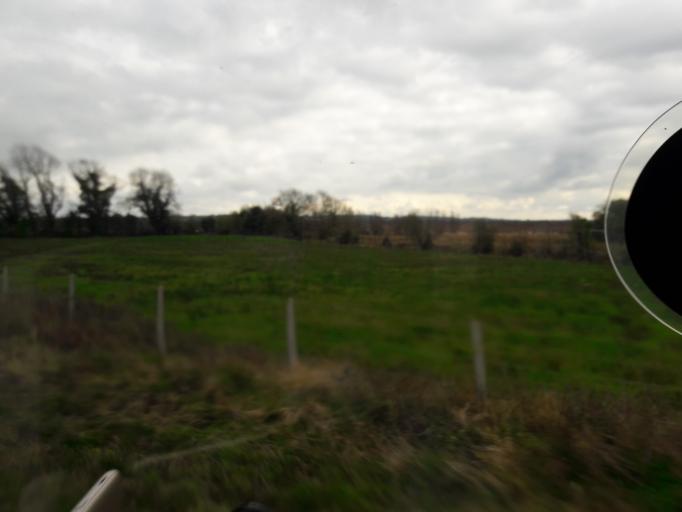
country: IE
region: Leinster
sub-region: An Longfort
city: Granard
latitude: 53.6623
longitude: -7.4584
